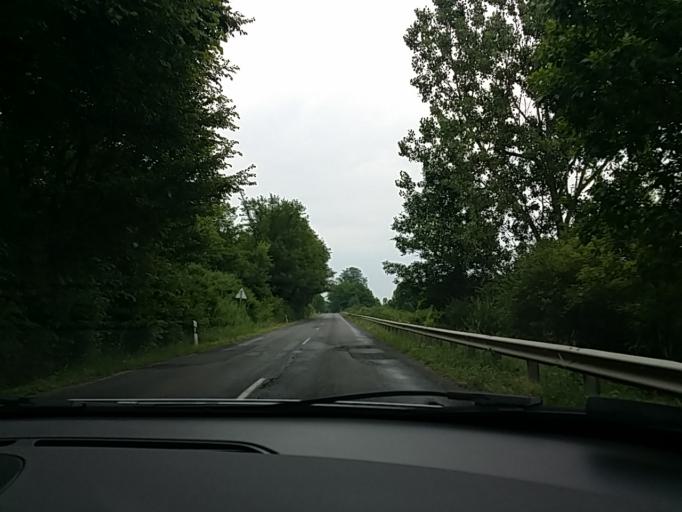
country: HU
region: Nograd
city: Batonyterenye
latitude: 47.9966
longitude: 19.8661
